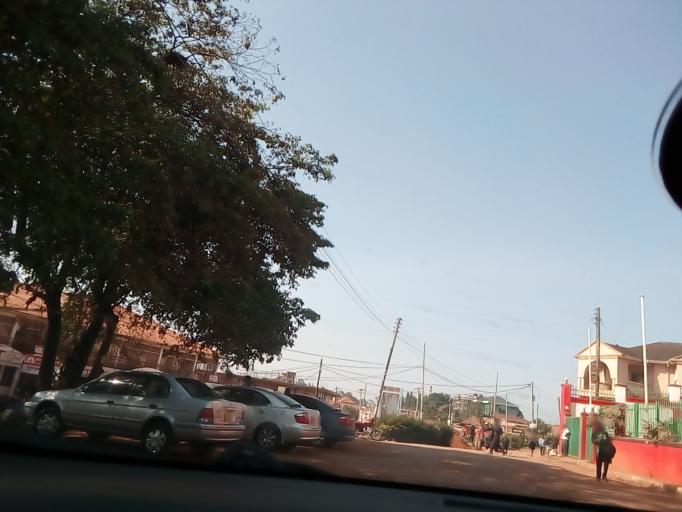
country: UG
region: Central Region
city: Masaka
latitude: -0.3419
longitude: 31.7368
